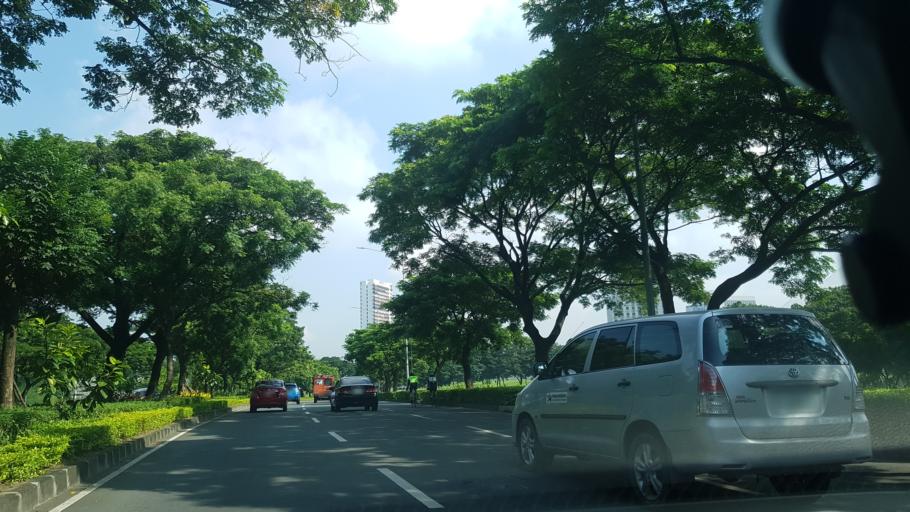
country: PH
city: Sambayanihan People's Village
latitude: 14.4144
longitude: 121.0343
